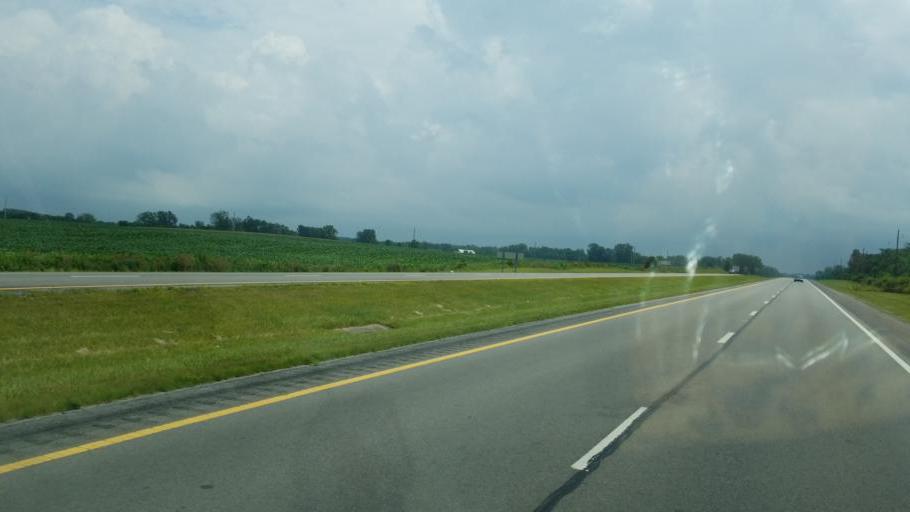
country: US
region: Ohio
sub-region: Logan County
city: Bellefontaine
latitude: 40.4286
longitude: -83.8010
